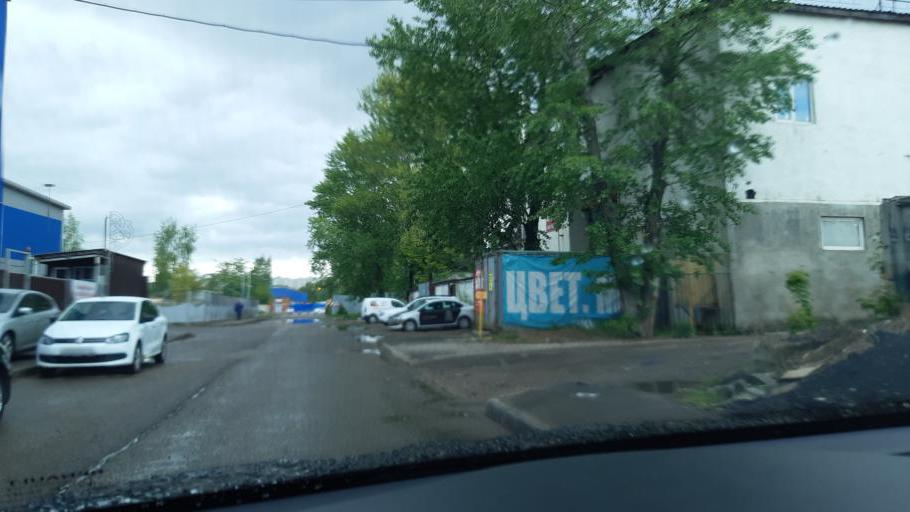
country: RU
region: Moskovskaya
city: Dolgoprudnyy
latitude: 55.9217
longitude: 37.5050
